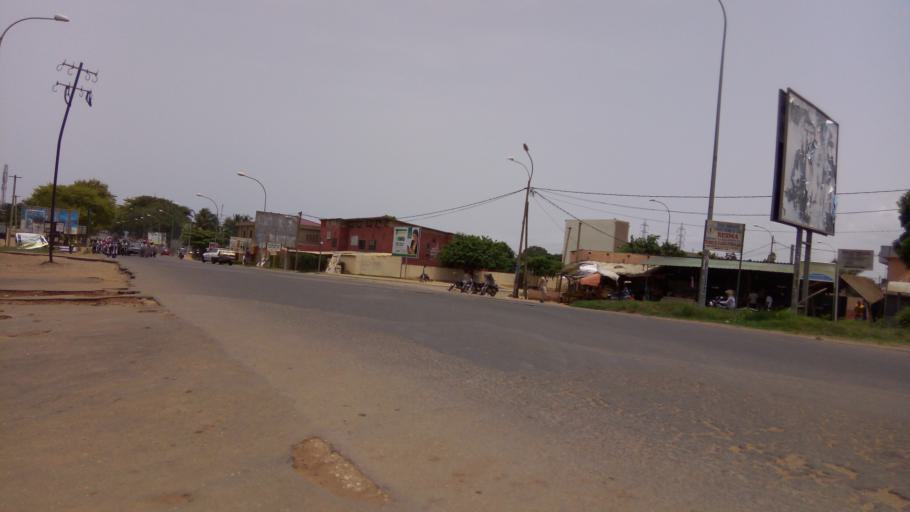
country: TG
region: Maritime
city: Lome
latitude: 6.1825
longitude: 1.2064
